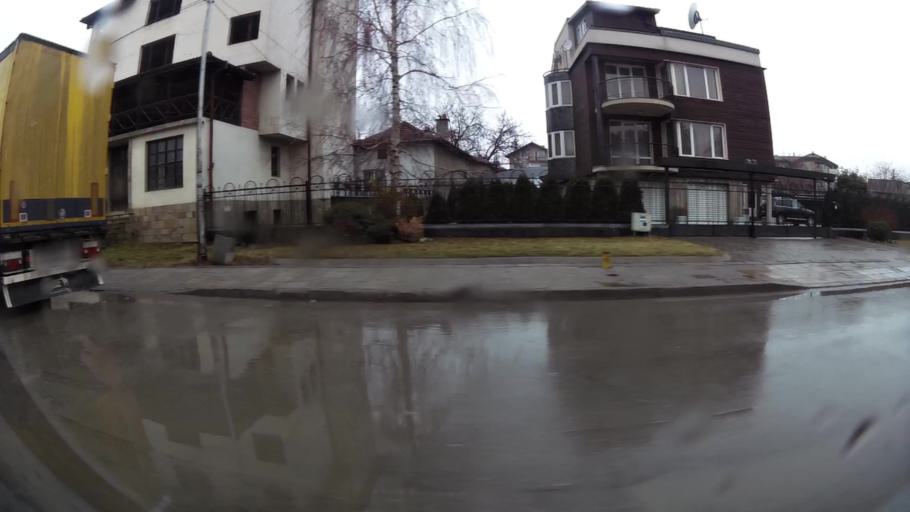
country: BG
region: Sofia-Capital
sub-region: Stolichna Obshtina
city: Sofia
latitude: 42.6258
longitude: 23.4066
